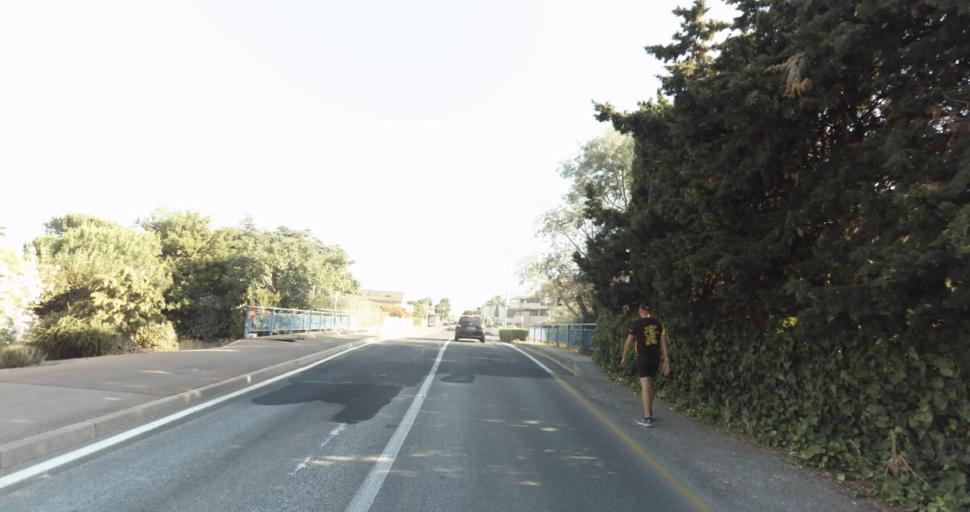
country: FR
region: Languedoc-Roussillon
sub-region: Departement des Pyrenees-Orientales
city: Saint-Cyprien-Plage
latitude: 42.6195
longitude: 3.0332
